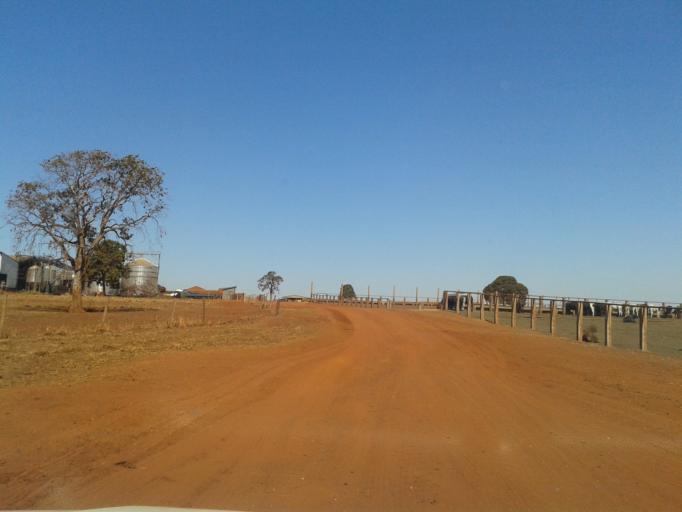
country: BR
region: Minas Gerais
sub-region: Santa Vitoria
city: Santa Vitoria
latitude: -19.2370
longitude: -50.2060
